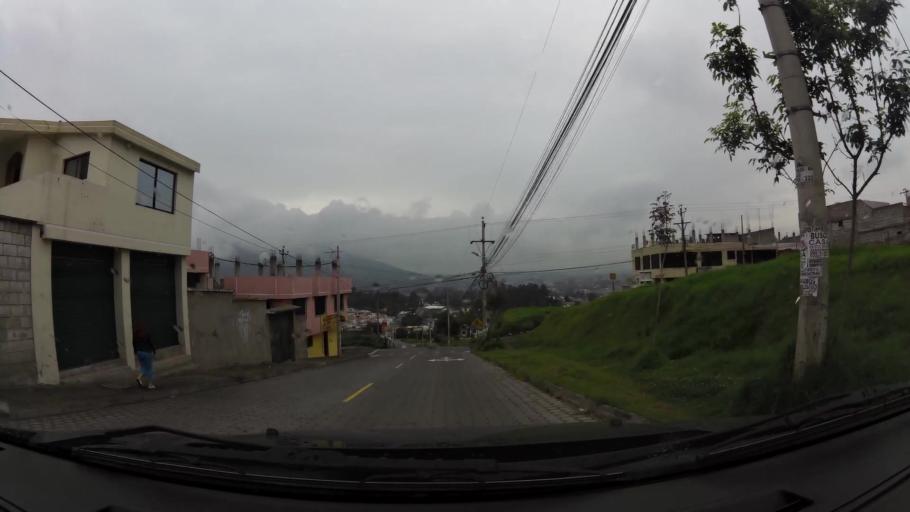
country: EC
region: Pichincha
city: Sangolqui
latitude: -0.2794
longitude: -78.4713
